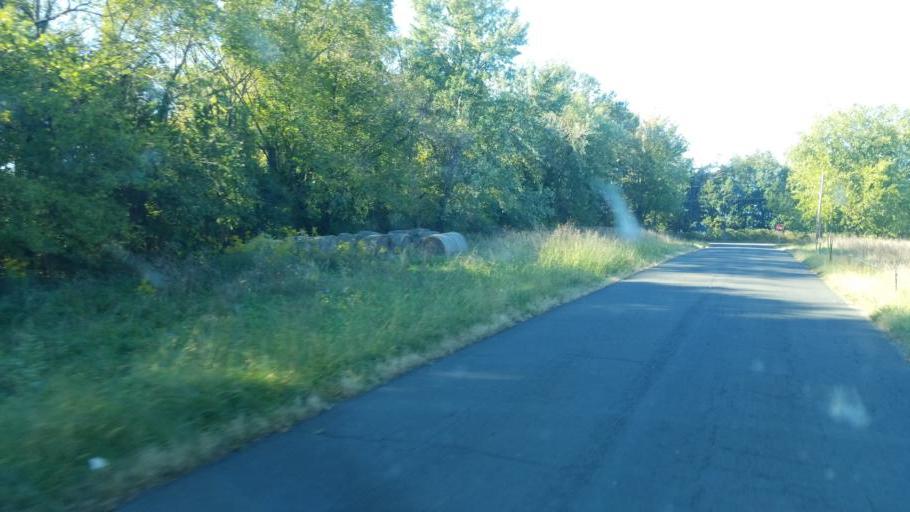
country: US
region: Virginia
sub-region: Fauquier County
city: Bealeton
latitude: 38.5373
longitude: -77.8164
